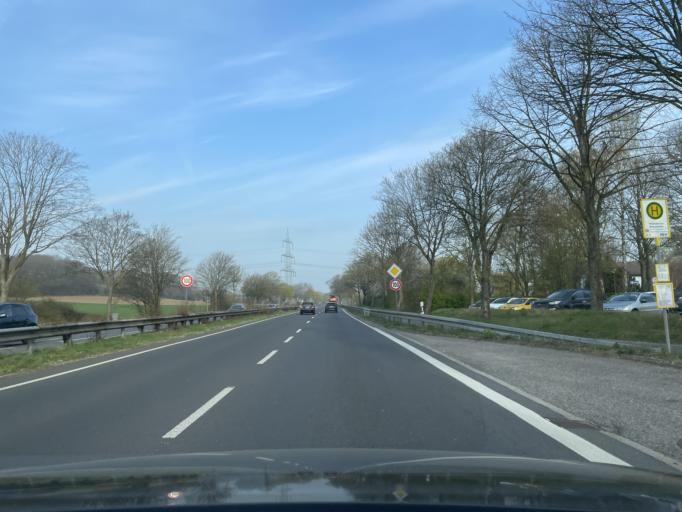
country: DE
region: North Rhine-Westphalia
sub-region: Regierungsbezirk Dusseldorf
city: Monchengladbach
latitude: 51.2257
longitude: 6.4309
